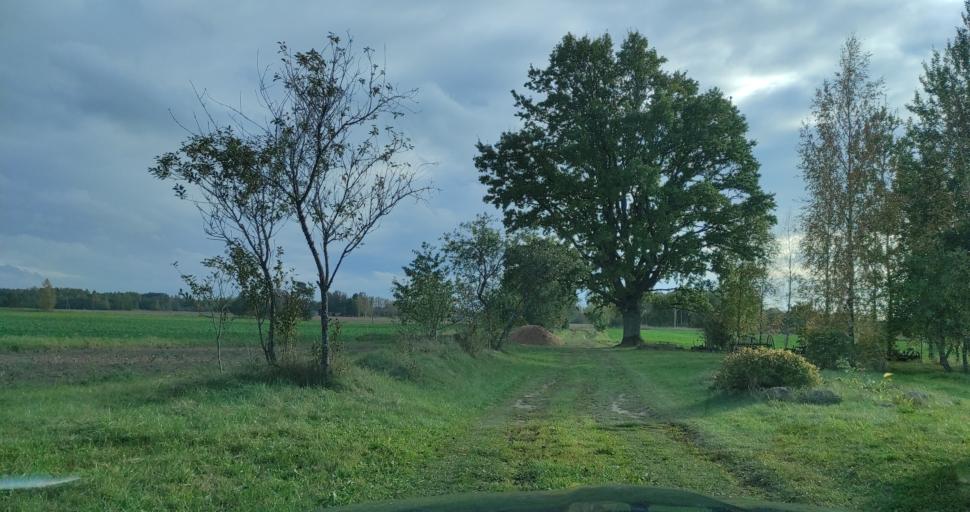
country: LV
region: Talsu Rajons
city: Sabile
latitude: 56.9030
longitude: 22.4215
